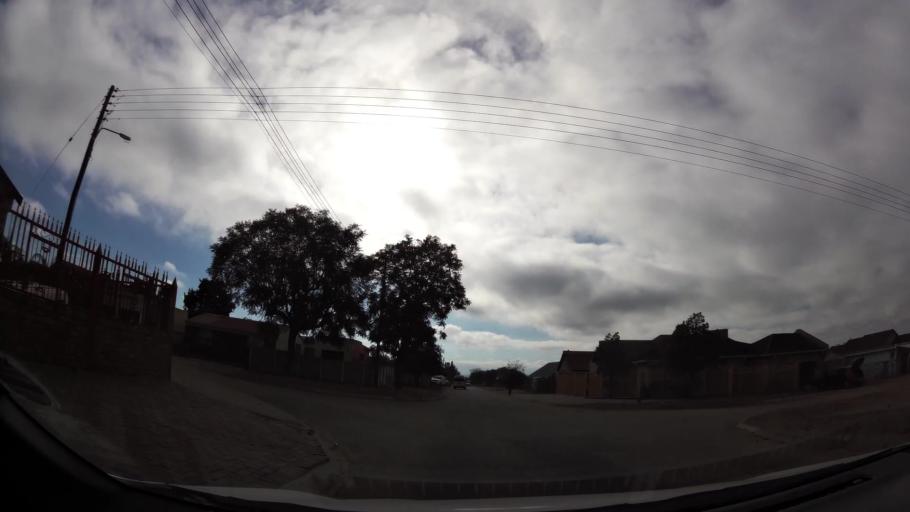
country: ZA
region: Limpopo
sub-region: Capricorn District Municipality
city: Polokwane
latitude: -23.8505
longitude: 29.3841
